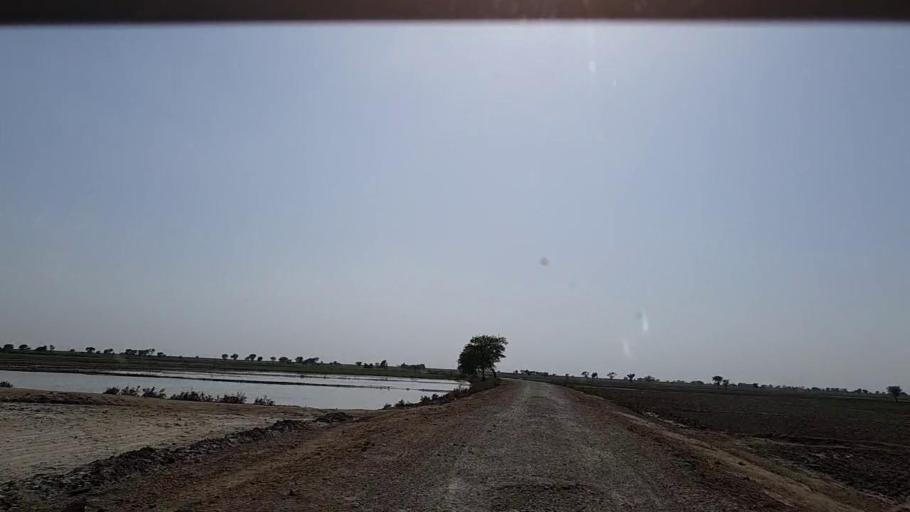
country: PK
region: Sindh
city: Phulji
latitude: 26.9217
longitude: 67.6675
